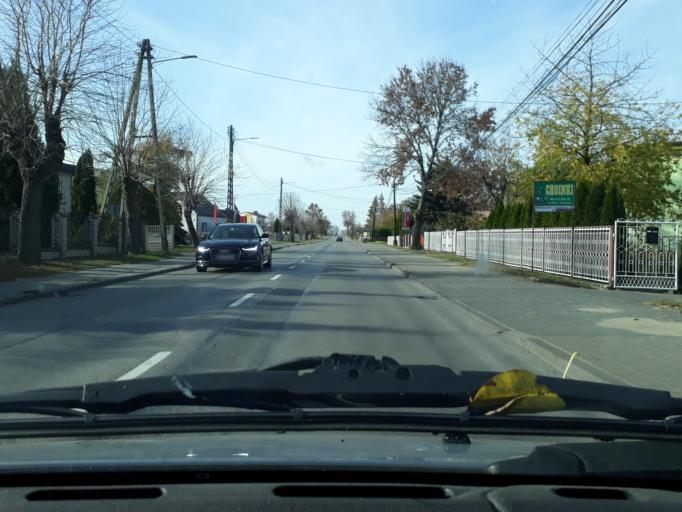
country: PL
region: Silesian Voivodeship
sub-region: Powiat myszkowski
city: Kozieglowy
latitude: 50.5988
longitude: 19.1437
